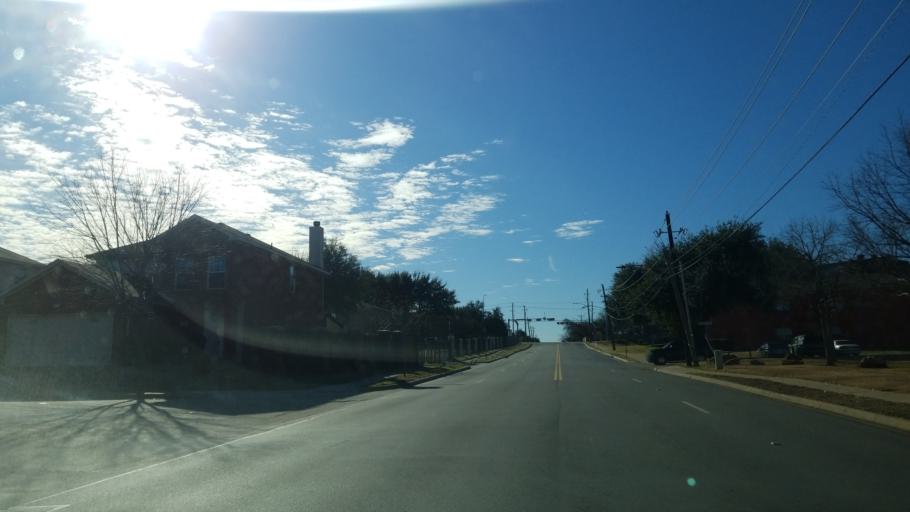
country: US
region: Texas
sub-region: Tarrant County
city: Arlington
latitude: 32.7225
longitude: -97.0572
